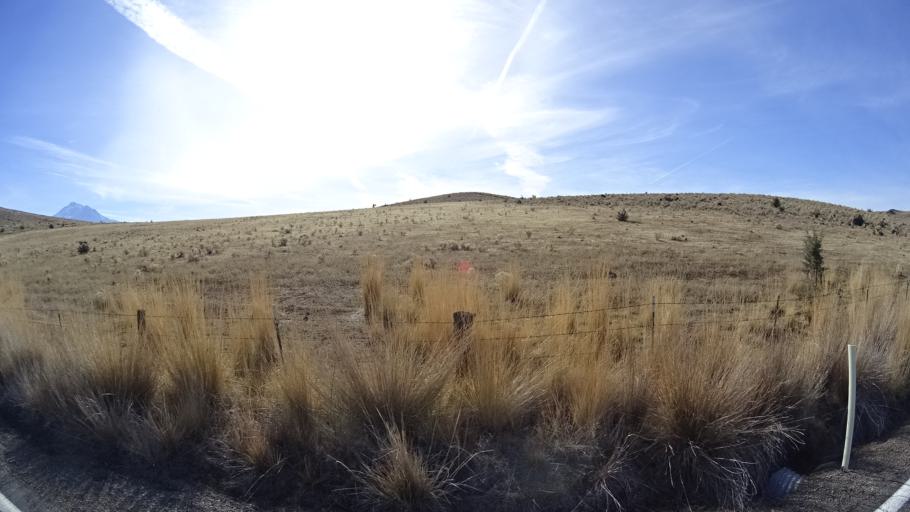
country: US
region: California
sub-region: Siskiyou County
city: Weed
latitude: 41.5493
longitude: -122.4944
